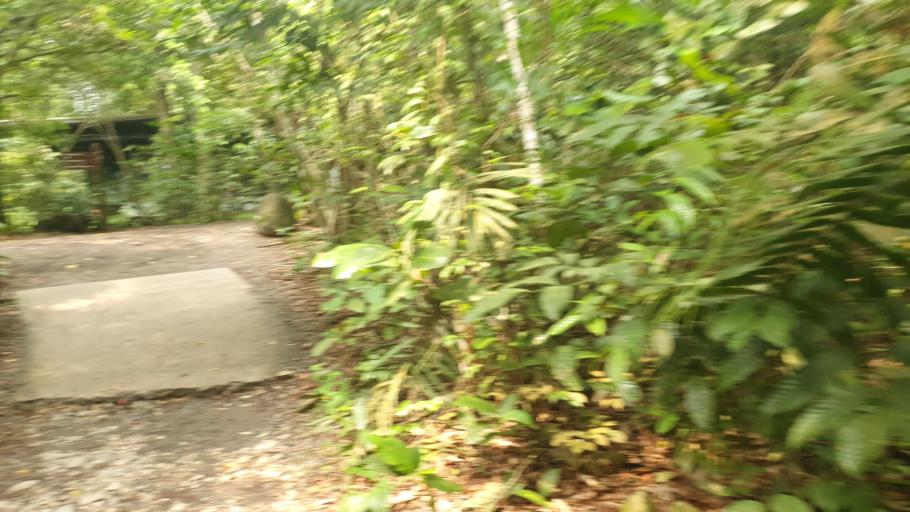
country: SG
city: Singapore
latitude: 1.3567
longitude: 103.8126
